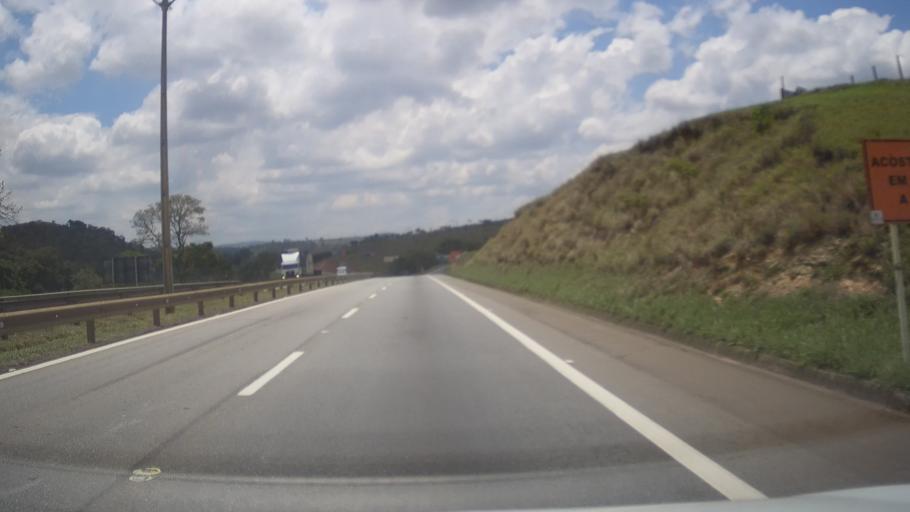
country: BR
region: Minas Gerais
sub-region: Tres Coracoes
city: Tres Coracoes
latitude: -21.6855
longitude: -45.3452
